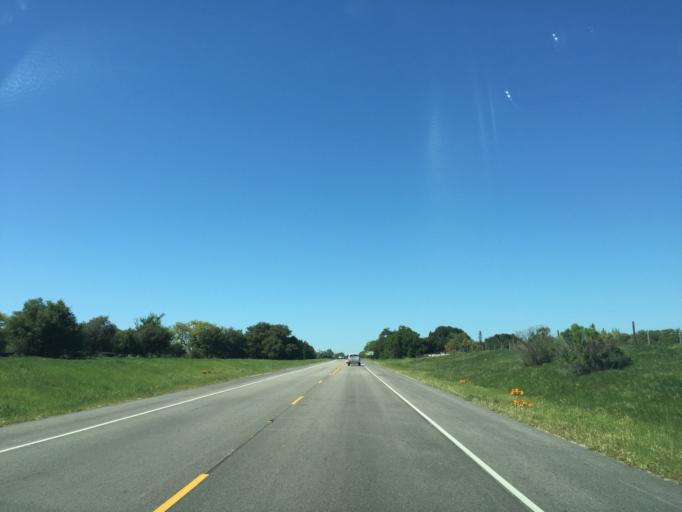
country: US
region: California
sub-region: Santa Barbara County
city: Los Olivos
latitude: 34.6464
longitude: -120.0918
